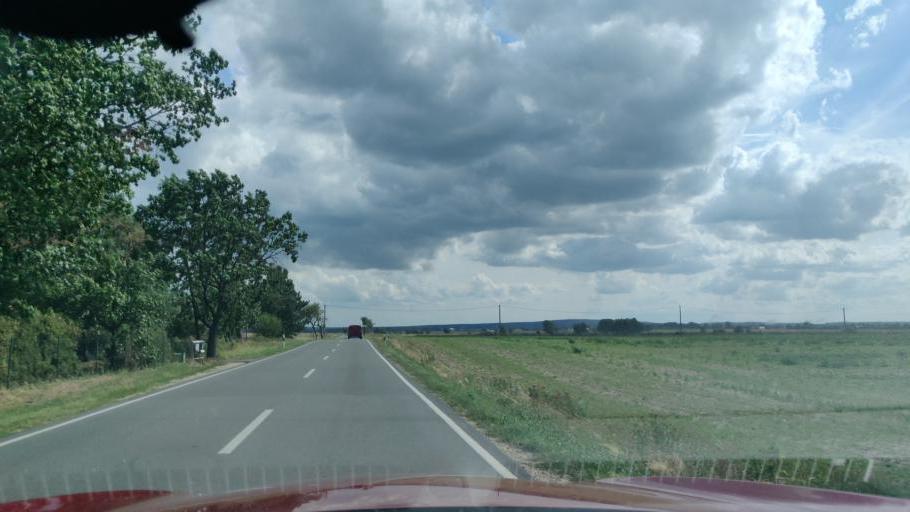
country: DE
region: Saxony
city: Schildau
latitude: 51.5107
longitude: 12.9098
